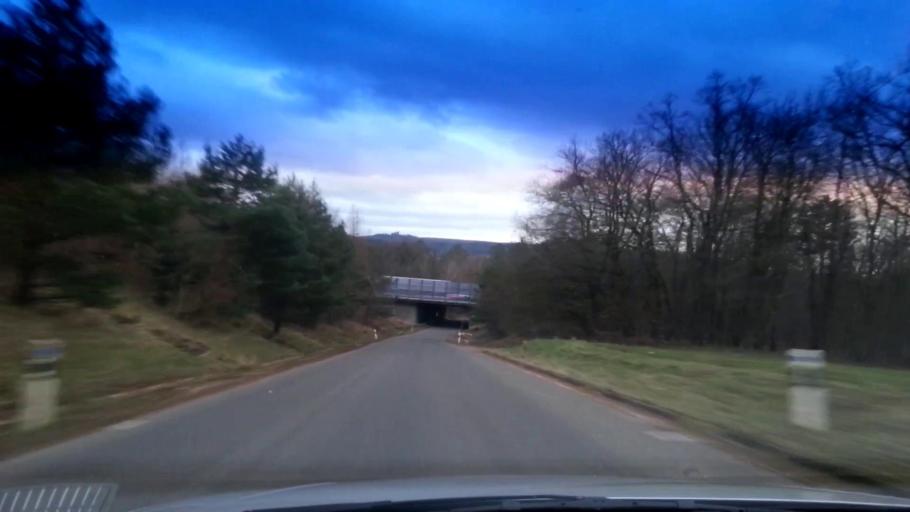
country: DE
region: Bavaria
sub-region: Upper Franconia
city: Schesslitz
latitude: 49.9836
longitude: 11.0625
